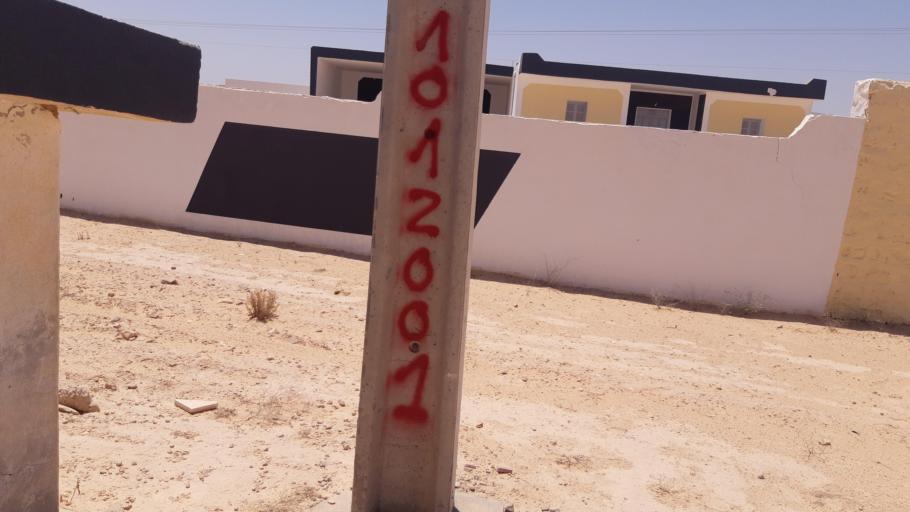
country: TN
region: Tataouine
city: Tataouine
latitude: 32.8518
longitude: 10.5336
